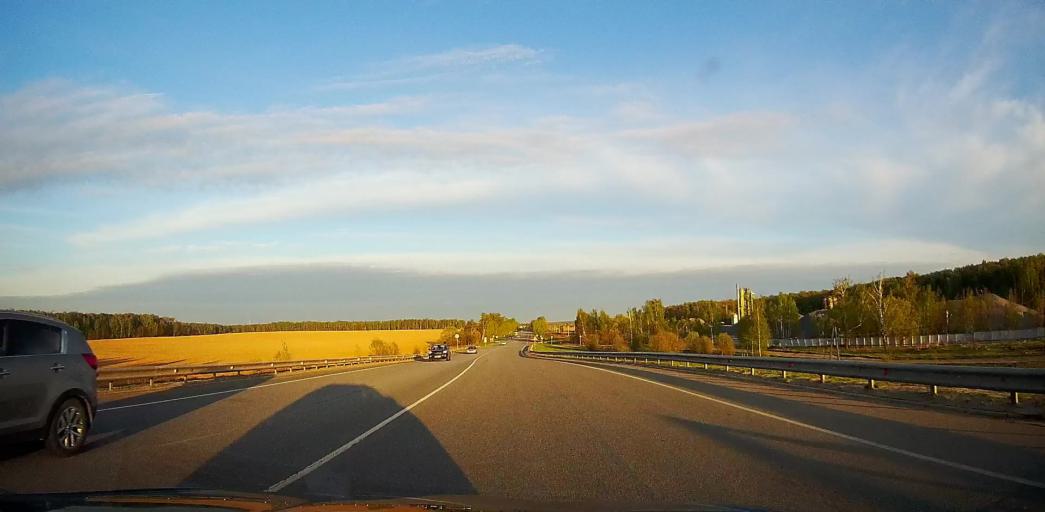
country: RU
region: Moskovskaya
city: Troitskoye
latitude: 55.2175
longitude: 38.5890
